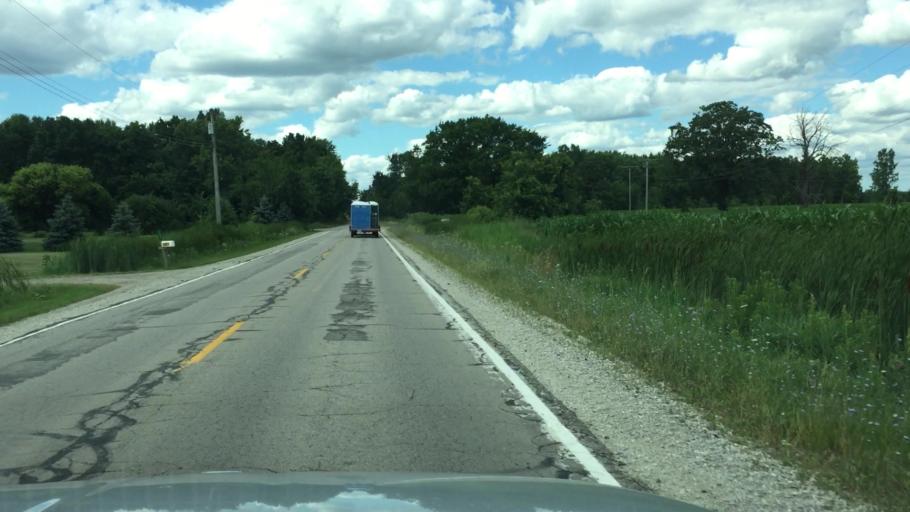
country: US
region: Michigan
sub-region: Saint Clair County
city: Capac
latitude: 42.9369
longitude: -82.9459
